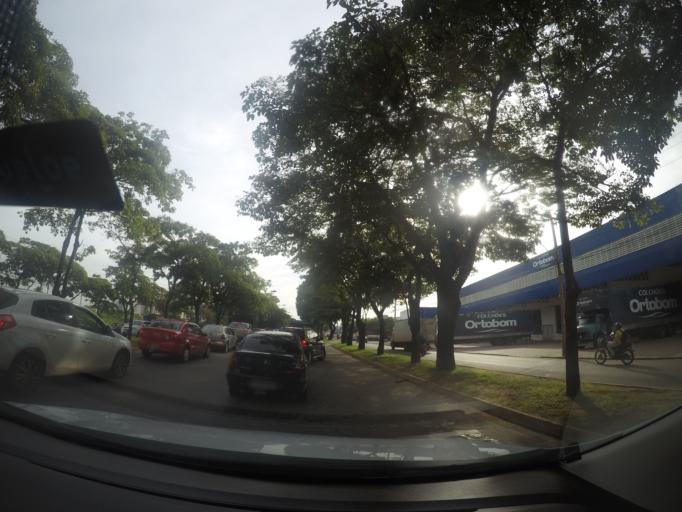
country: BR
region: Goias
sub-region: Goiania
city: Goiania
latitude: -16.6982
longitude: -49.3298
